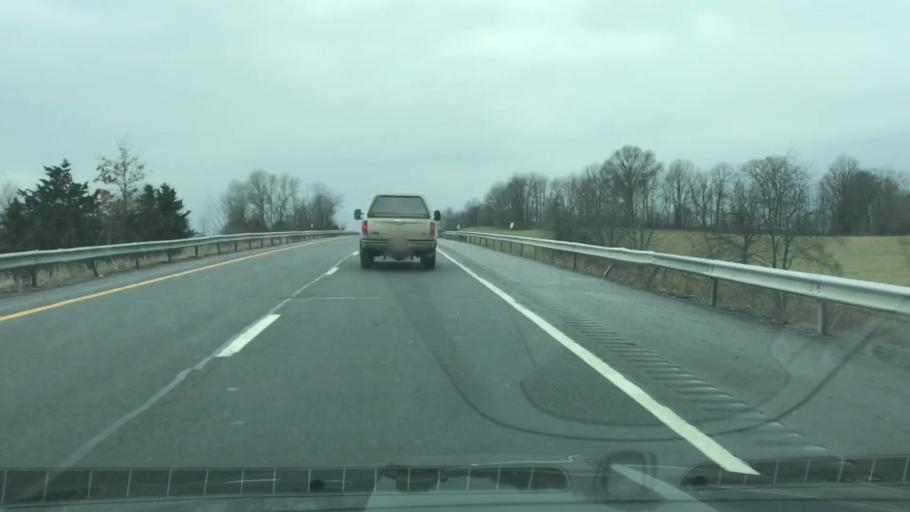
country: US
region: New York
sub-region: Orange County
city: Montgomery
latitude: 41.5008
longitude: -74.2394
